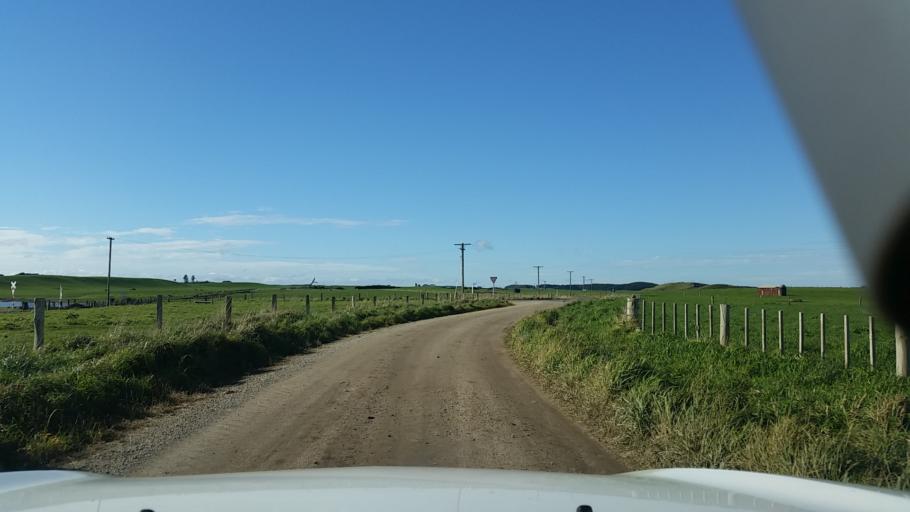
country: NZ
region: Taranaki
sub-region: South Taranaki District
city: Patea
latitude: -39.7743
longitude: 174.5518
